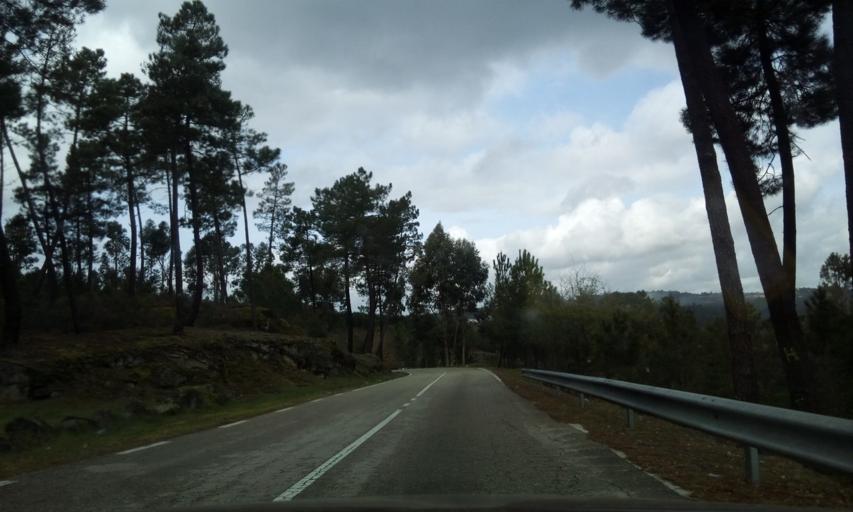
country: PT
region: Viseu
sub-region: Satao
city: Satao
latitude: 40.6598
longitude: -7.6639
